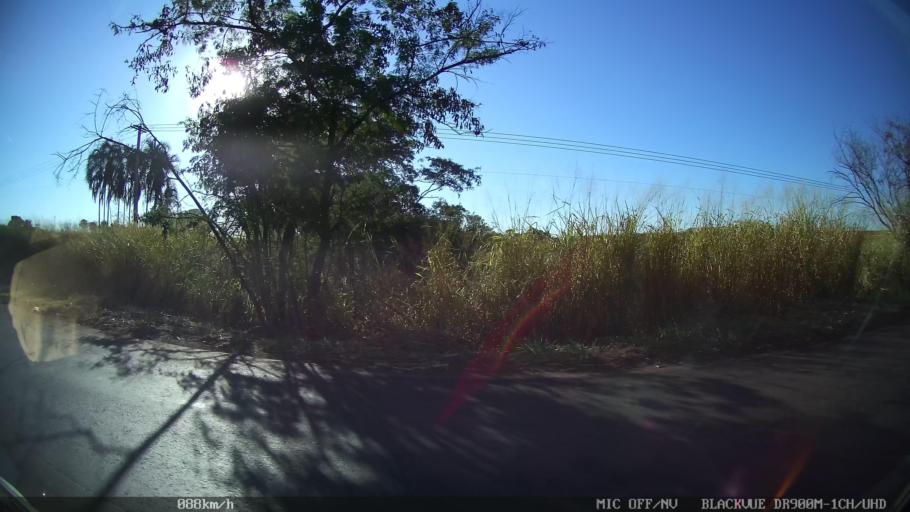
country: BR
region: Sao Paulo
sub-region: Olimpia
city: Olimpia
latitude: -20.7018
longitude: -48.9421
